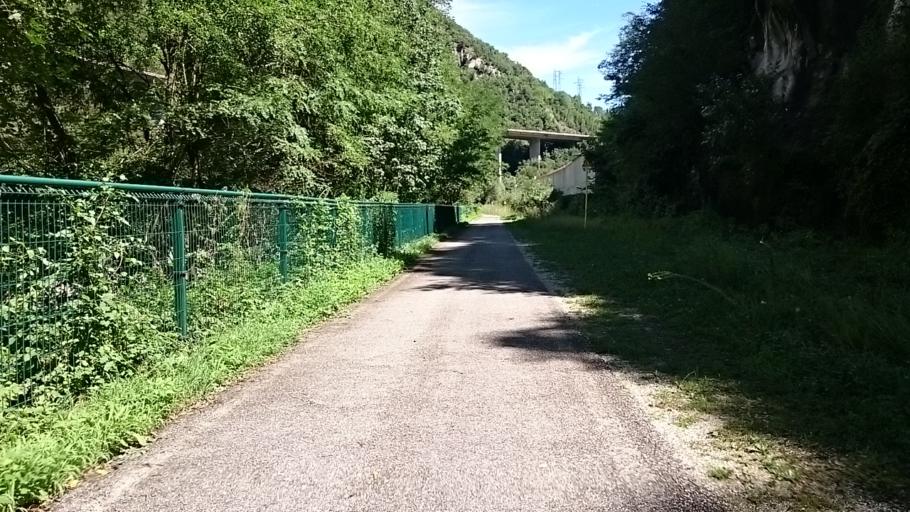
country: IT
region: Trentino-Alto Adige
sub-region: Bolzano
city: Collalbo
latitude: 46.5097
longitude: 11.4690
